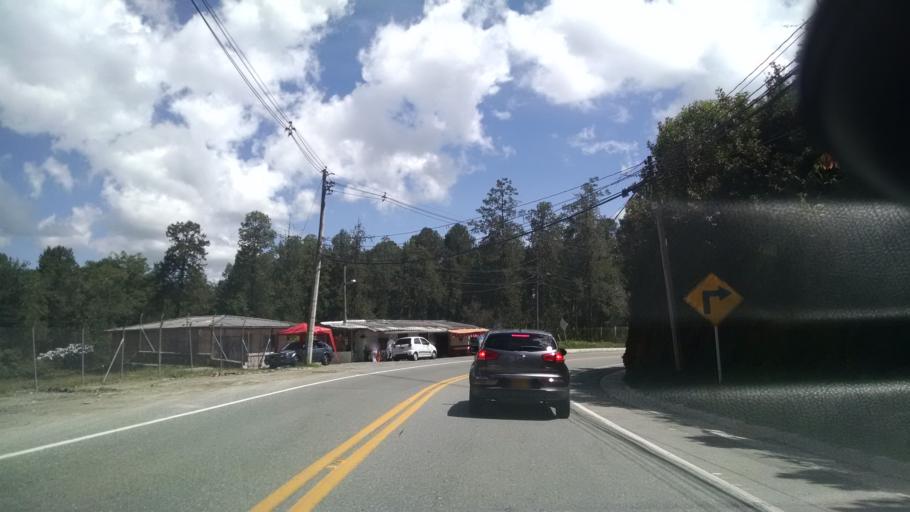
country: CO
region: Antioquia
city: El Retiro
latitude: 6.1112
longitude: -75.5009
